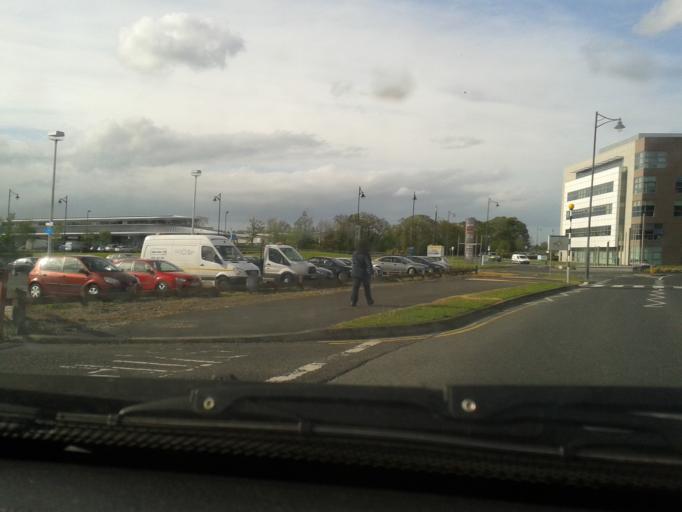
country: IE
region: Leinster
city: Ballymun
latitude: 53.4023
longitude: -6.2586
